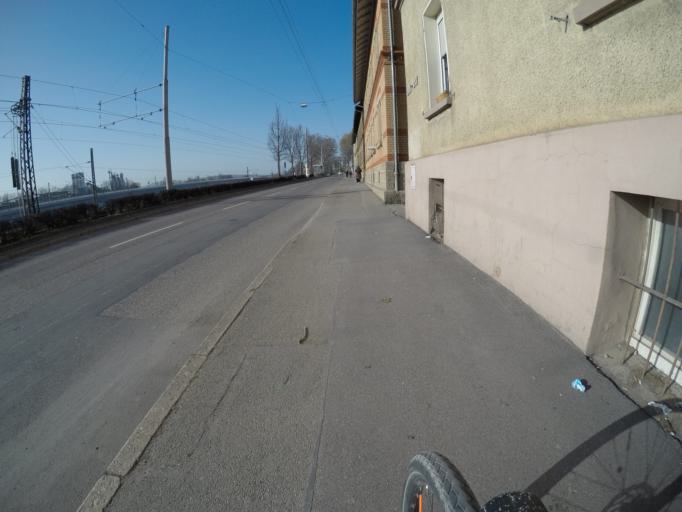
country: DE
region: Baden-Wuerttemberg
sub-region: Regierungsbezirk Stuttgart
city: Stuttgart-Ost
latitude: 48.7922
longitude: 9.2432
